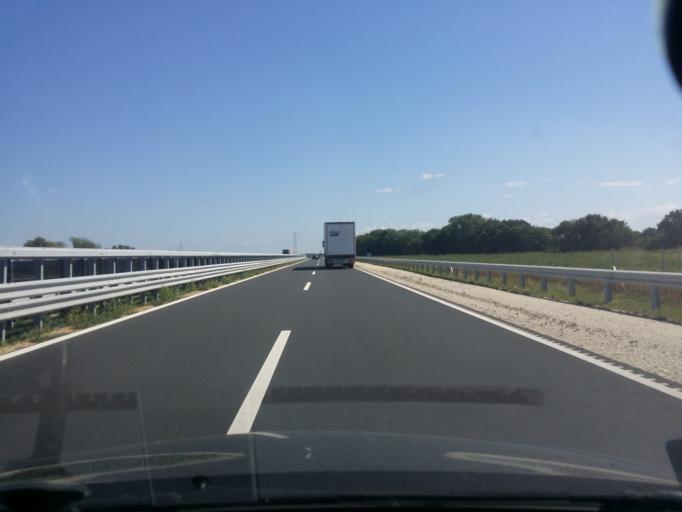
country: HU
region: Vas
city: Repcelak
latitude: 47.3879
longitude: 16.9831
